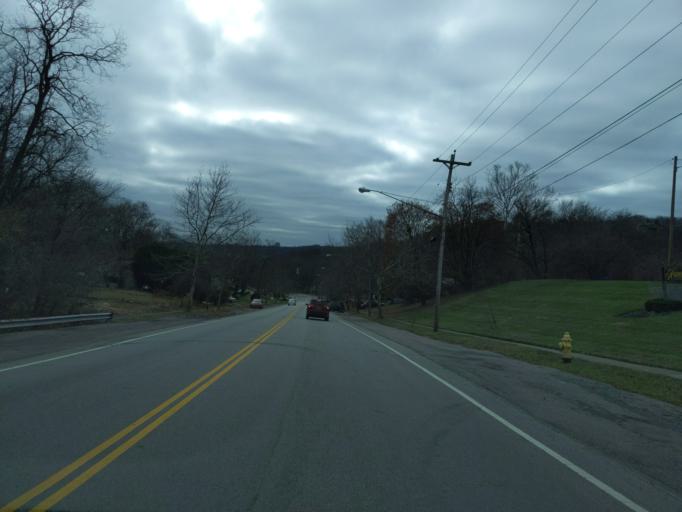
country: US
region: Ohio
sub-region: Hamilton County
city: Finneytown
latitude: 39.1776
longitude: -84.5464
